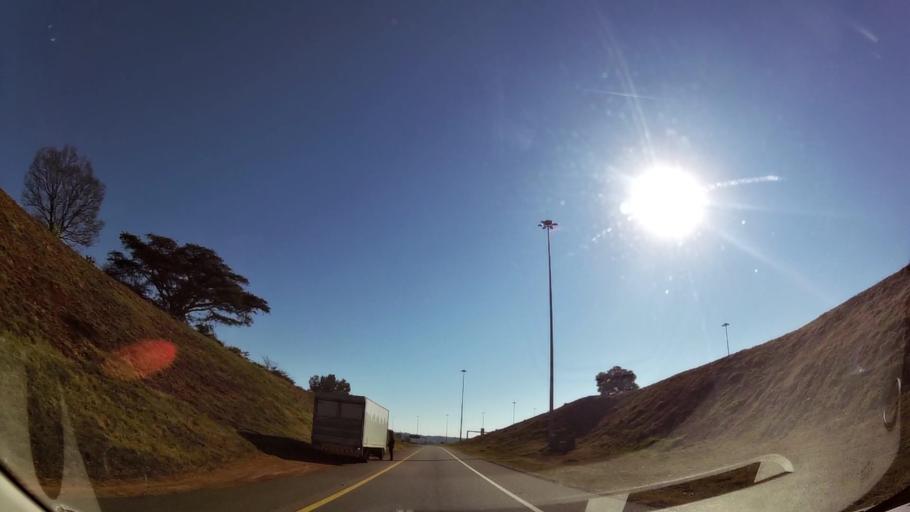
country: ZA
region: Gauteng
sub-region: City of Tshwane Metropolitan Municipality
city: Centurion
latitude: -25.8289
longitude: 28.2417
